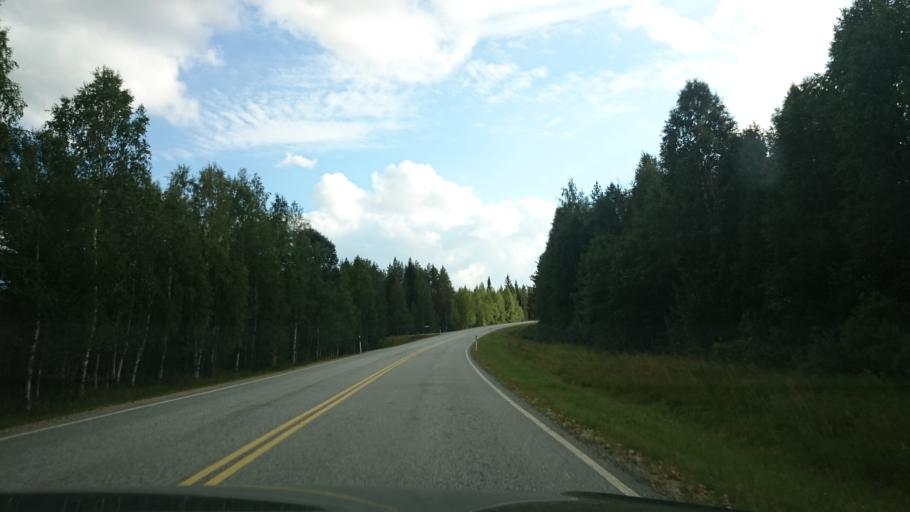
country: FI
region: Kainuu
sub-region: Kehys-Kainuu
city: Kuhmo
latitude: 64.5188
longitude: 29.9462
